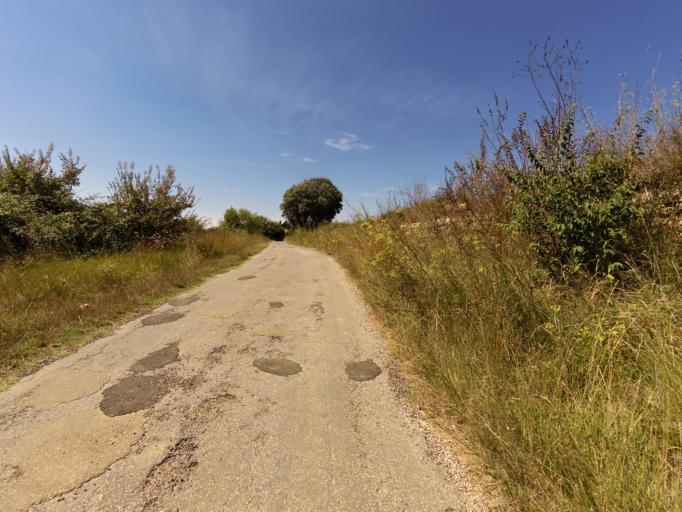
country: FR
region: Languedoc-Roussillon
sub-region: Departement du Gard
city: Aubais
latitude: 43.7536
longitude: 4.1290
